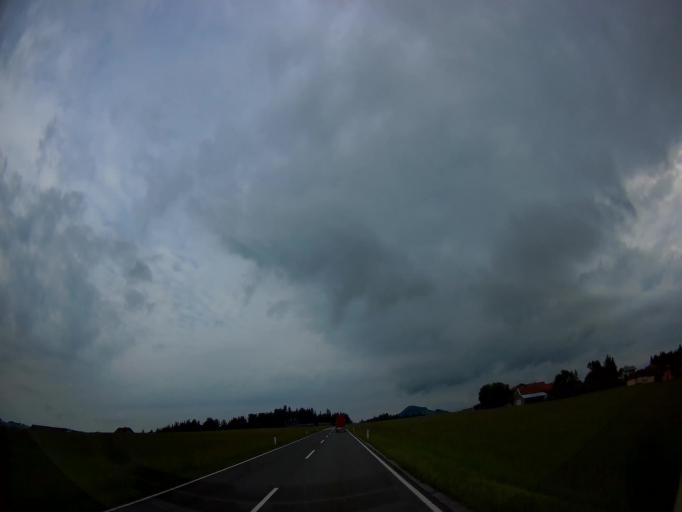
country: AT
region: Salzburg
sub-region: Politischer Bezirk Salzburg-Umgebung
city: Obertrum am See
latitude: 47.9025
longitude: 13.0792
